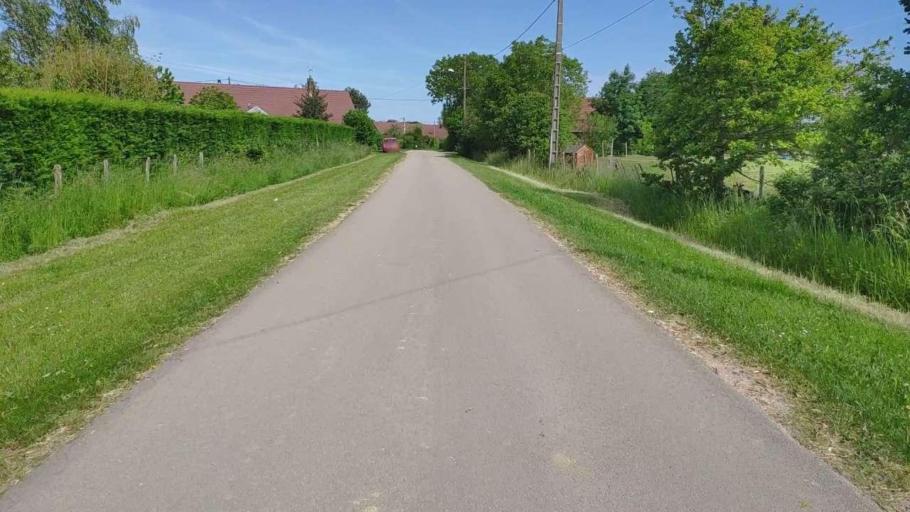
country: FR
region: Franche-Comte
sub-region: Departement du Jura
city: Bletterans
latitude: 46.7083
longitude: 5.4468
